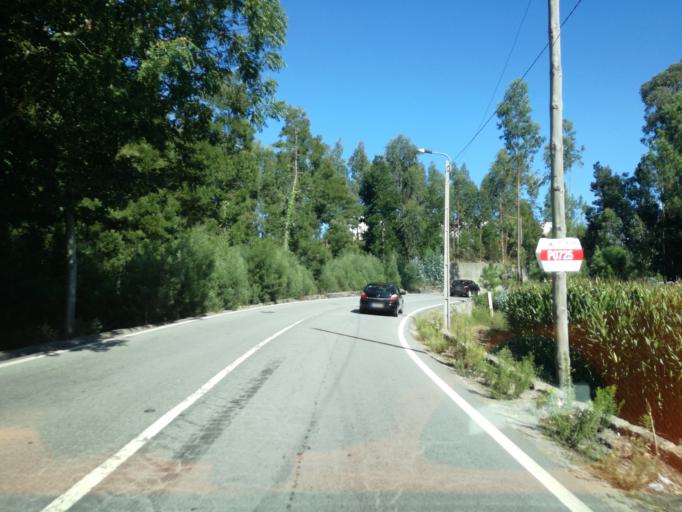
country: PT
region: Porto
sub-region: Maia
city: Anta
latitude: 41.2864
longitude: -8.5992
